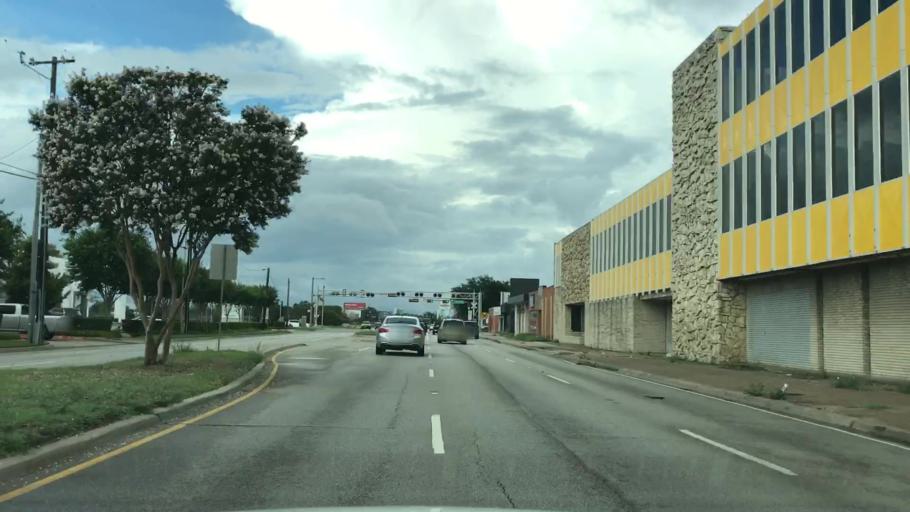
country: US
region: Texas
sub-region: Dallas County
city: University Park
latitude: 32.8292
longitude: -96.8429
